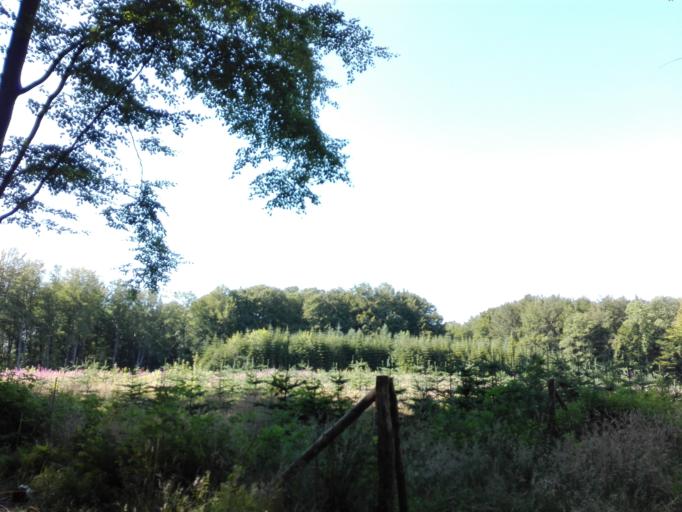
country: DK
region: Central Jutland
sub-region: Odder Kommune
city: Odder
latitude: 55.9683
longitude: 10.1252
